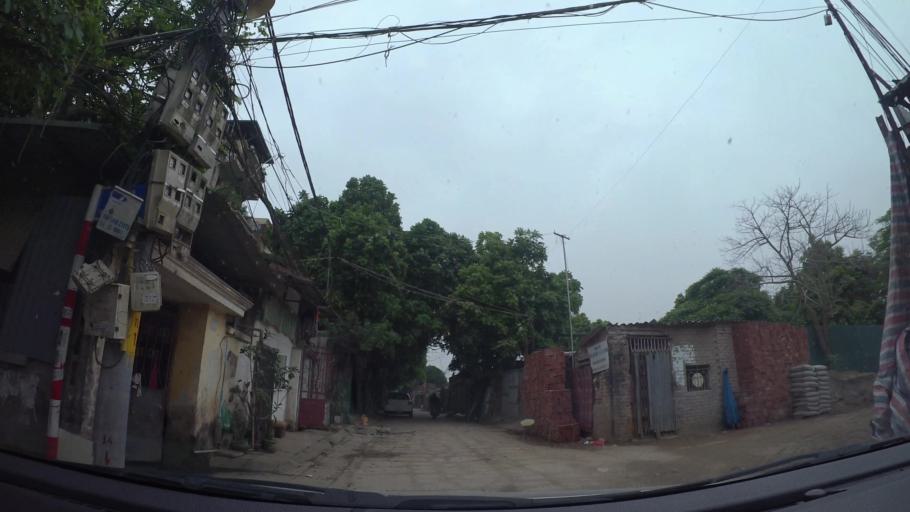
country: VN
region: Ha Noi
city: Tay Ho
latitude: 21.0643
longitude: 105.8377
